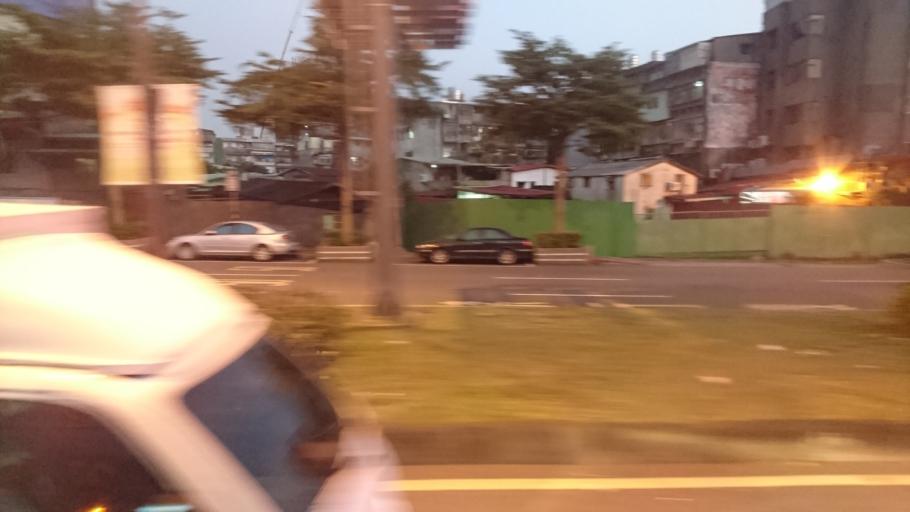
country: TW
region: Taipei
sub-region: Taipei
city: Banqiao
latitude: 25.0321
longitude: 121.4951
